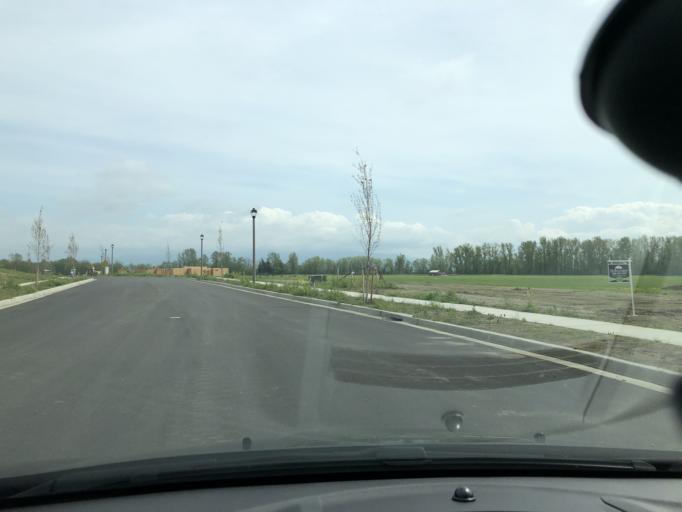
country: US
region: Washington
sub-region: Whatcom County
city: Lynden
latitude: 48.9342
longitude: -122.4709
